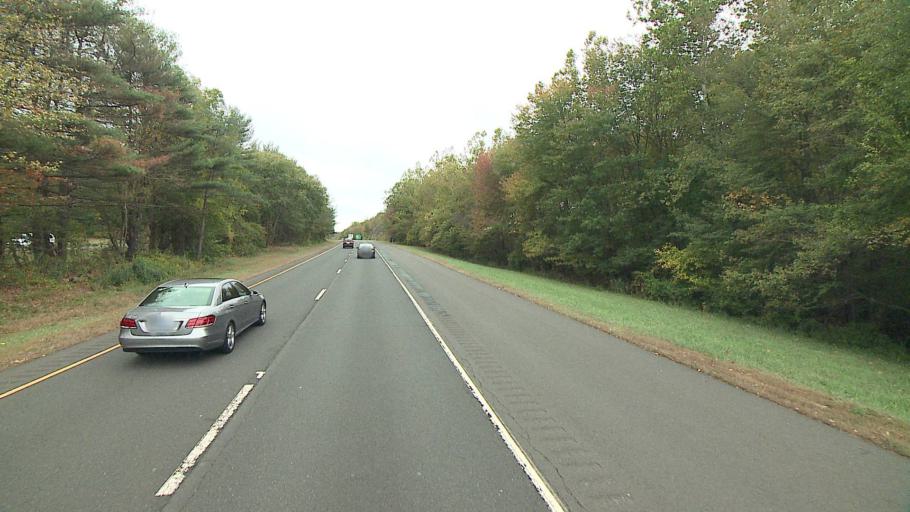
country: US
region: Connecticut
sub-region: Middlesex County
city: Higganum
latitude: 41.4899
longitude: -72.5670
